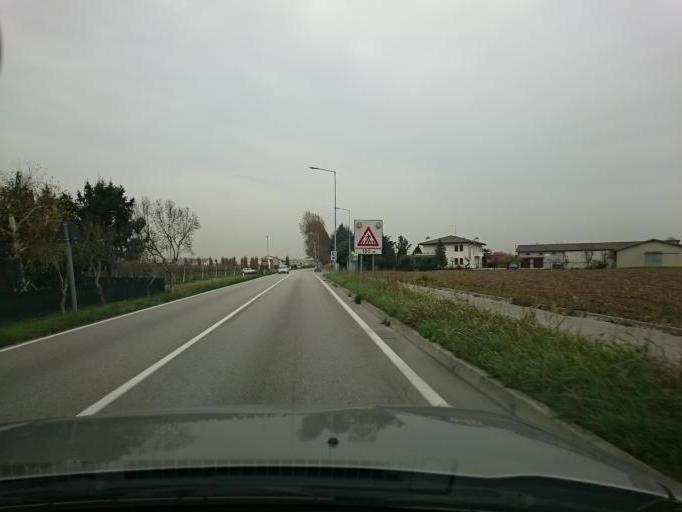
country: IT
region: Veneto
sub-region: Provincia di Padova
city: Masera di Padova
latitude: 45.3070
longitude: 11.8656
